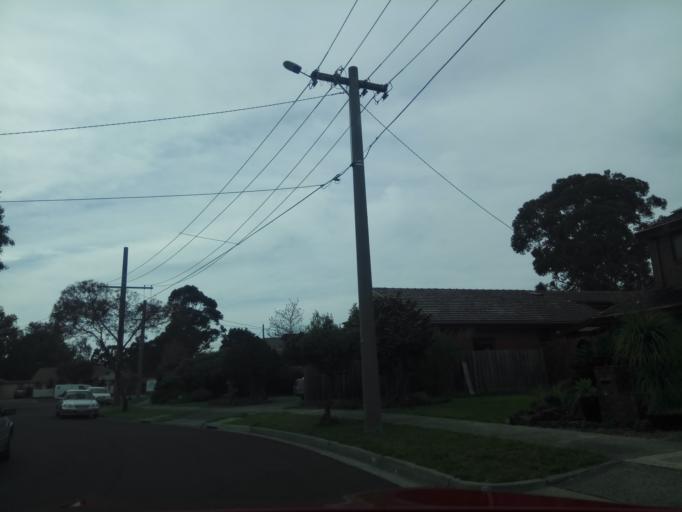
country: AU
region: Victoria
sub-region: Greater Dandenong
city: Springvale South
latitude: -37.9635
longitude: 145.1468
